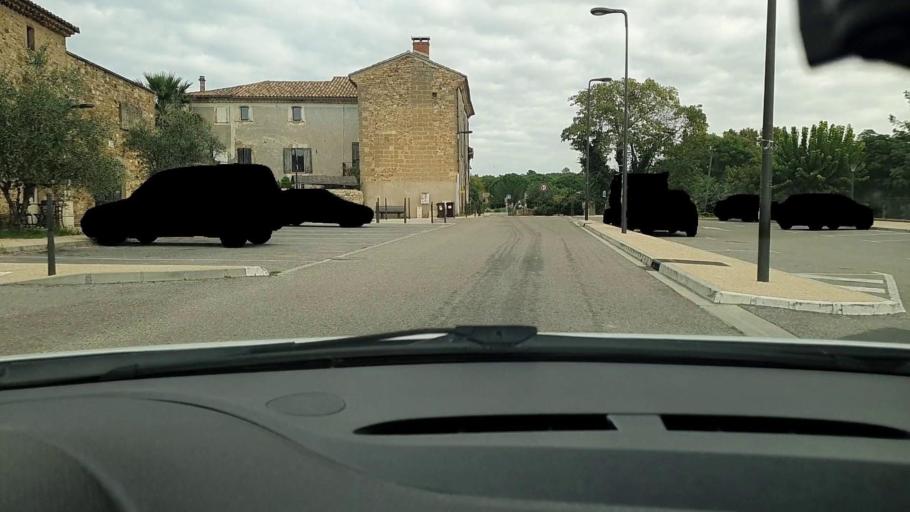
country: FR
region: Languedoc-Roussillon
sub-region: Departement du Gard
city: Saint-Chaptes
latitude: 44.0426
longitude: 4.2984
